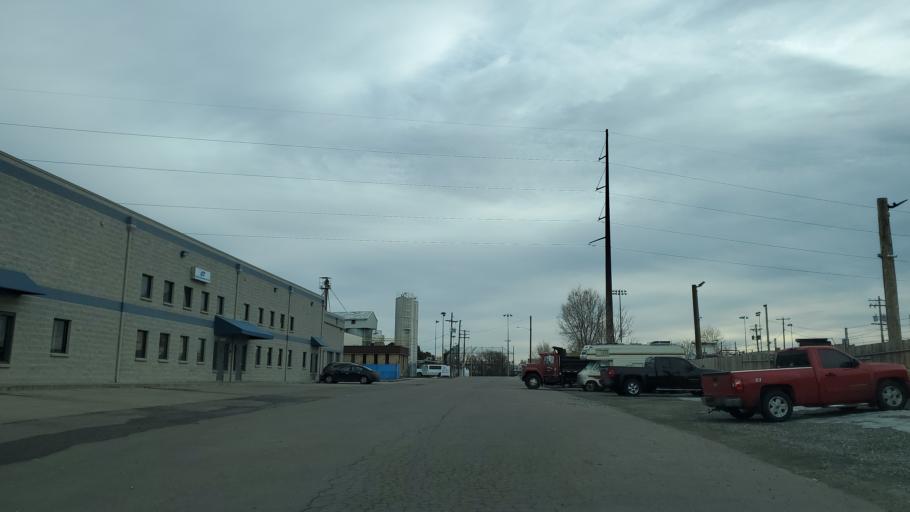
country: US
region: Colorado
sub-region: Denver County
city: Denver
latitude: 39.7139
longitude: -105.0061
